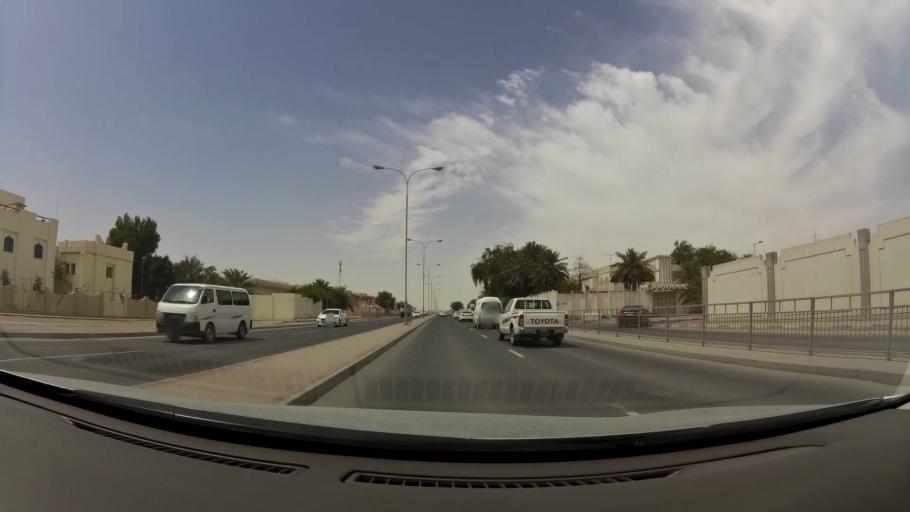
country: QA
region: Baladiyat ar Rayyan
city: Ar Rayyan
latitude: 25.2860
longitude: 51.4279
